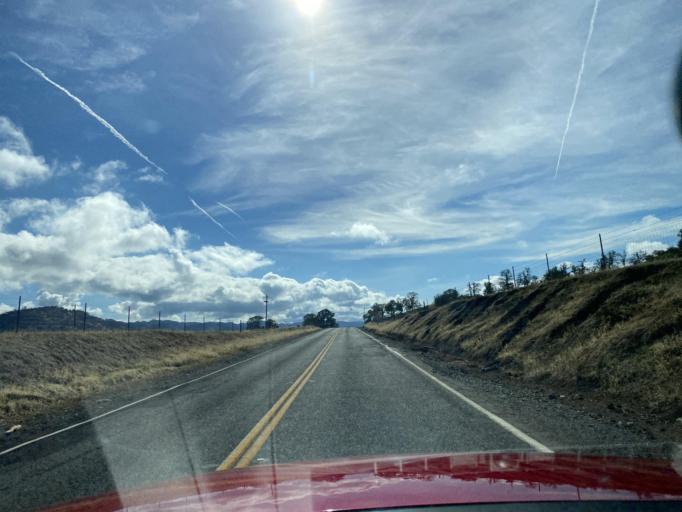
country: US
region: California
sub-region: Glenn County
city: Willows
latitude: 39.4763
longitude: -122.5143
